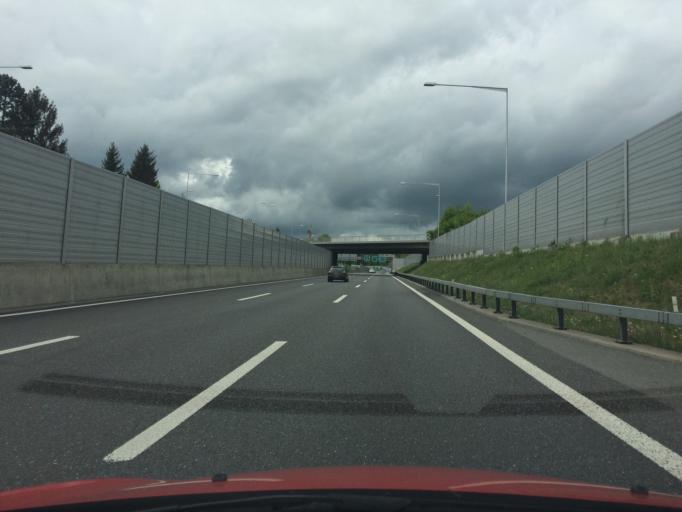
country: CH
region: Lucerne
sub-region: Hochdorf District
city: Emmen
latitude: 47.0826
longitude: 8.2814
